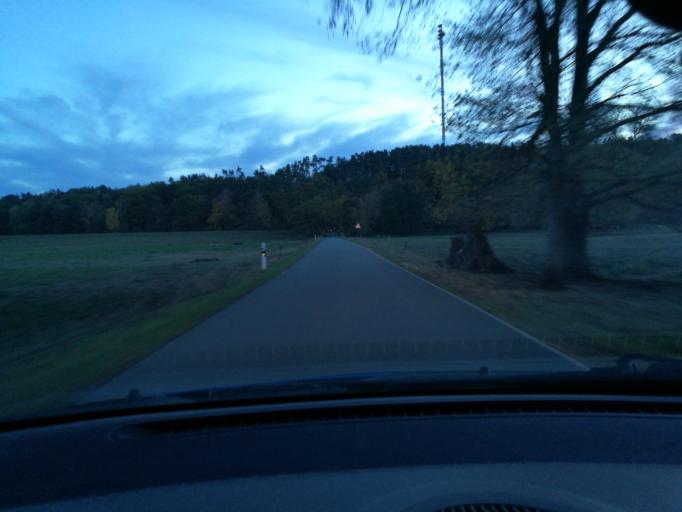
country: DE
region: Brandenburg
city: Lenzen
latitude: 53.0740
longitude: 11.4501
